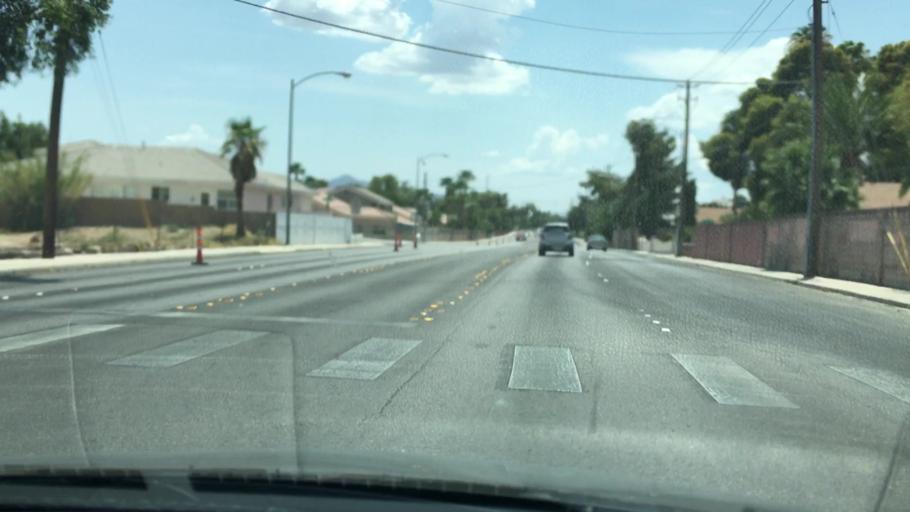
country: US
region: Nevada
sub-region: Clark County
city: Whitney
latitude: 36.0893
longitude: -115.0915
